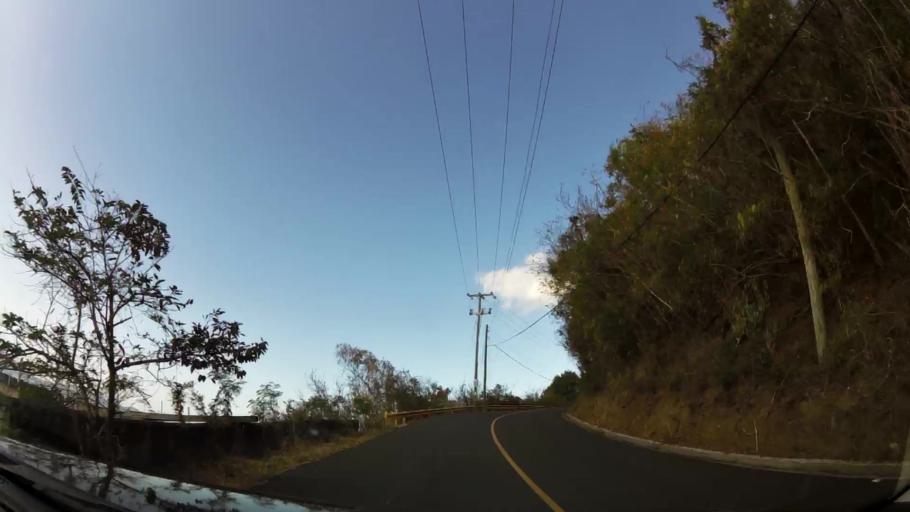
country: VG
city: Road Town
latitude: 18.4033
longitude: -64.6764
